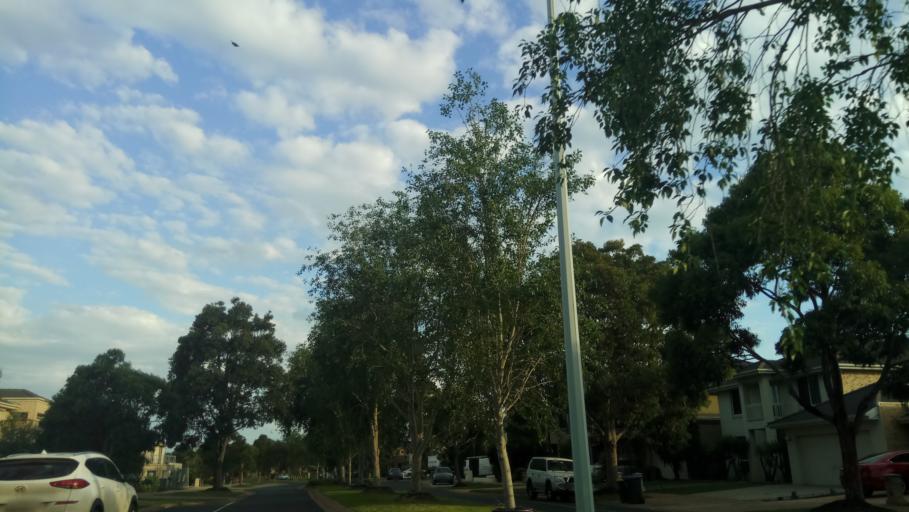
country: AU
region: Victoria
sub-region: Wyndham
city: Point Cook
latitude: -37.9024
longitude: 144.7630
